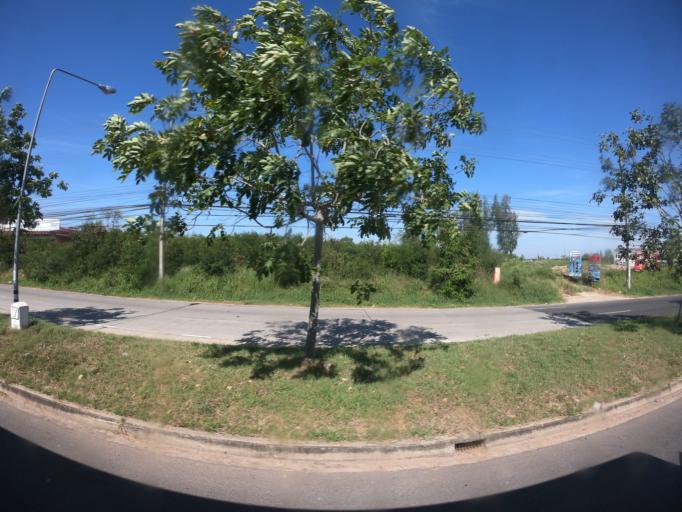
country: TH
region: Nakhon Ratchasima
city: Nakhon Ratchasima
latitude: 15.0084
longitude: 102.1241
